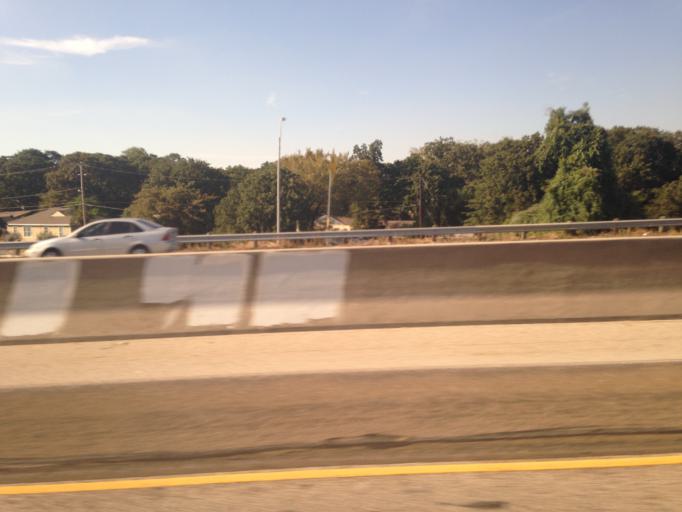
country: US
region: Texas
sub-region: Tarrant County
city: Haltom City
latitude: 32.7785
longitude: -97.2800
